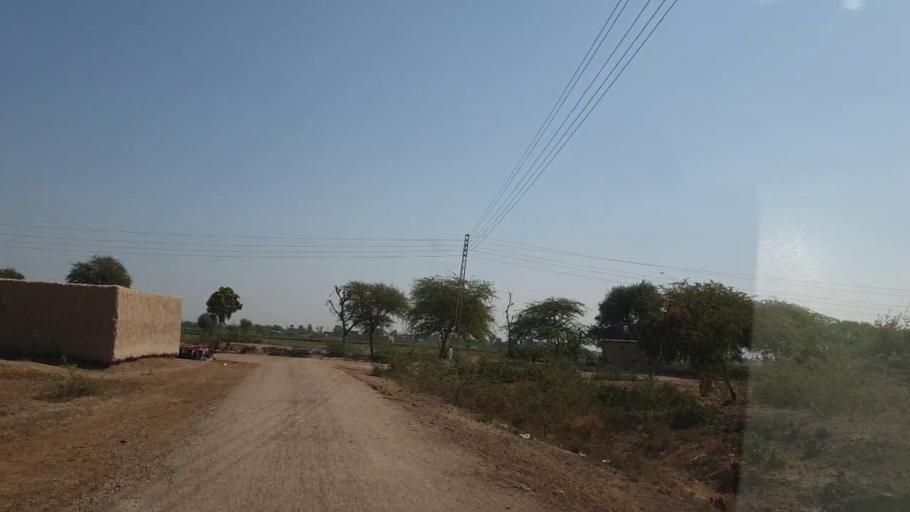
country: PK
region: Sindh
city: Kunri
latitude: 25.1680
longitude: 69.5308
